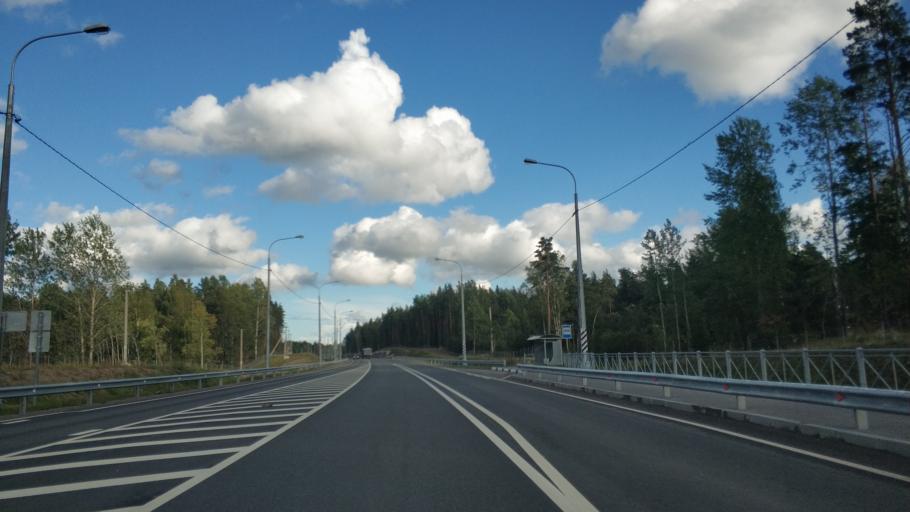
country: RU
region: Leningrad
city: Kuznechnoye
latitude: 61.0967
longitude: 29.9798
